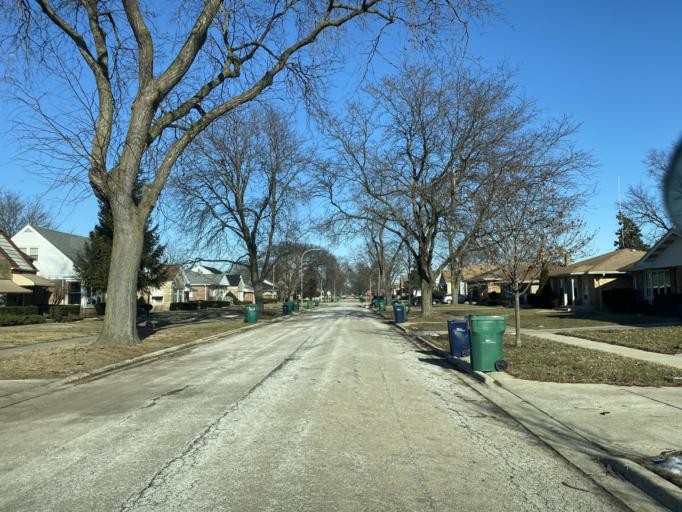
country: US
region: Illinois
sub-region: Cook County
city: Westchester
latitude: 41.8515
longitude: -87.8720
